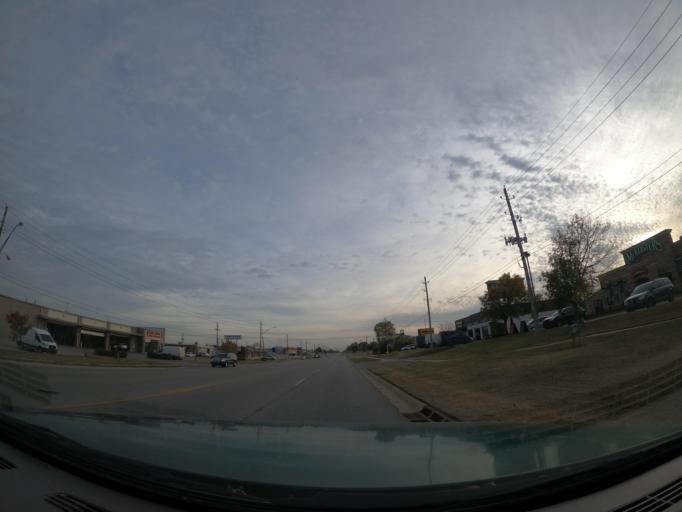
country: US
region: Oklahoma
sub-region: Tulsa County
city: Broken Arrow
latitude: 36.0584
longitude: -95.8154
